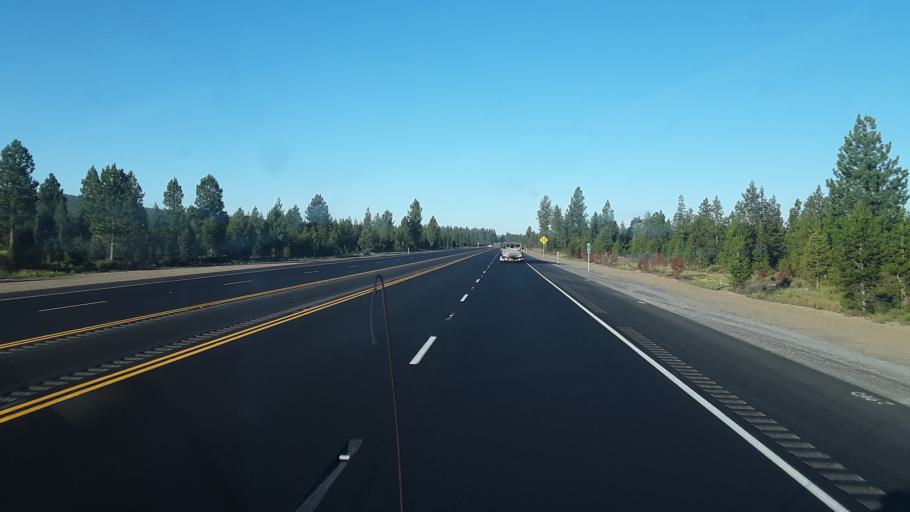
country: US
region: Oregon
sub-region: Deschutes County
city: La Pine
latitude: 43.5055
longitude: -121.6637
